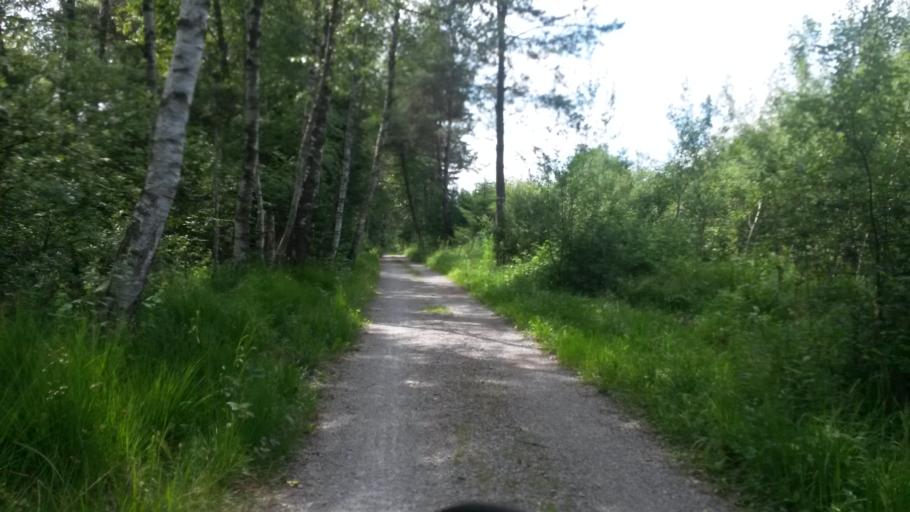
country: DE
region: Bavaria
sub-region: Upper Bavaria
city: Bernau am Chiemsee
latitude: 47.8136
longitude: 12.4071
